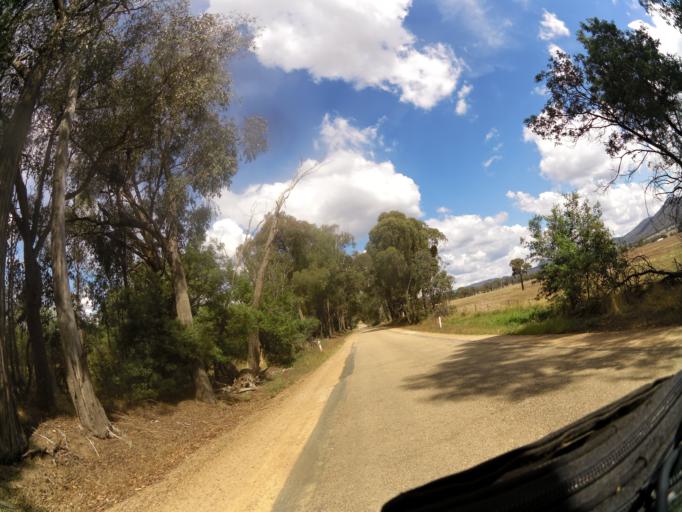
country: AU
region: Victoria
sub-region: Benalla
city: Benalla
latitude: -36.7713
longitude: 145.9750
